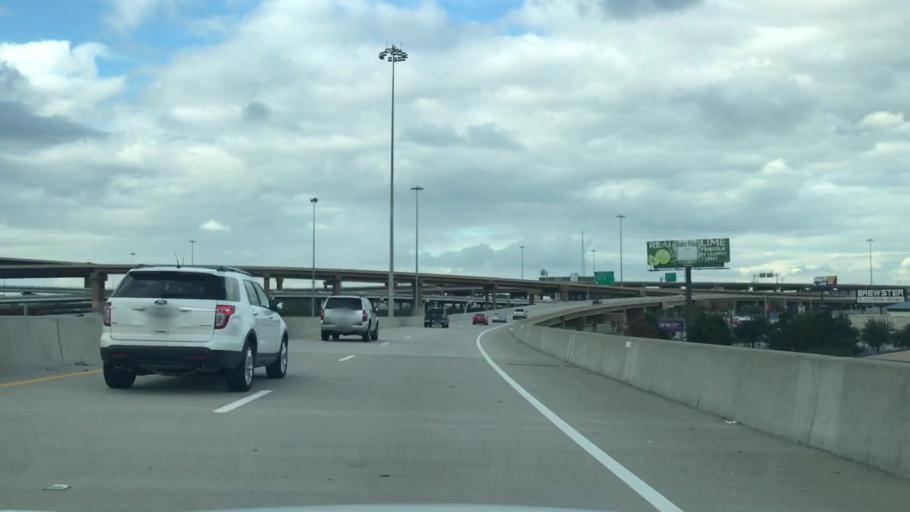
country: US
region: Texas
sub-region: Dallas County
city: Farmers Branch
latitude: 32.9043
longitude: -96.8969
